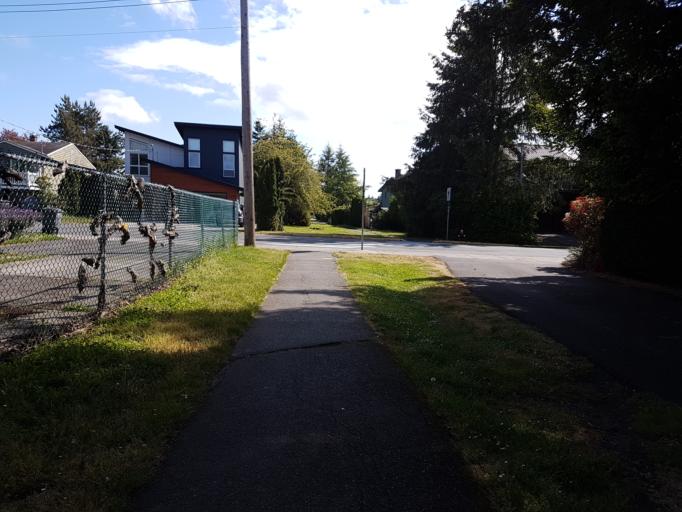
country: CA
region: British Columbia
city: Oak Bay
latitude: 48.4869
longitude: -123.3341
